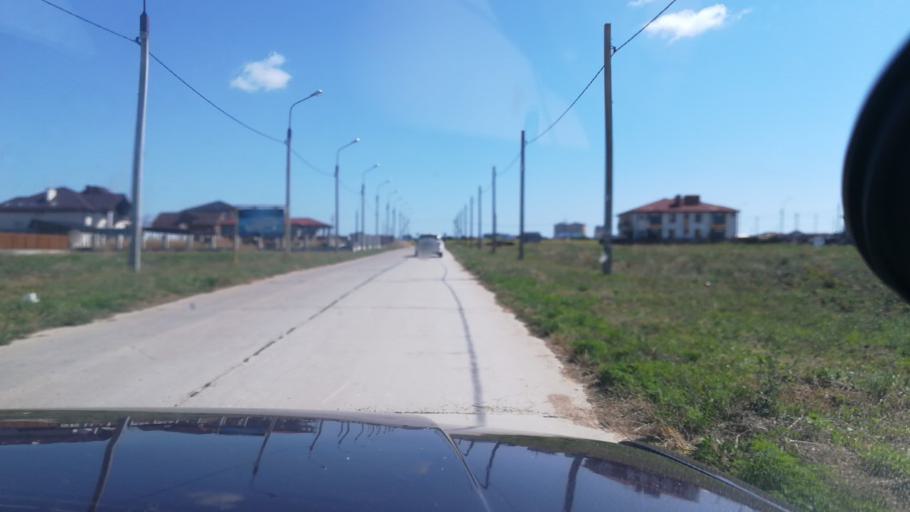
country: RU
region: Krasnodarskiy
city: Vityazevo
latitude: 44.9903
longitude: 37.2755
